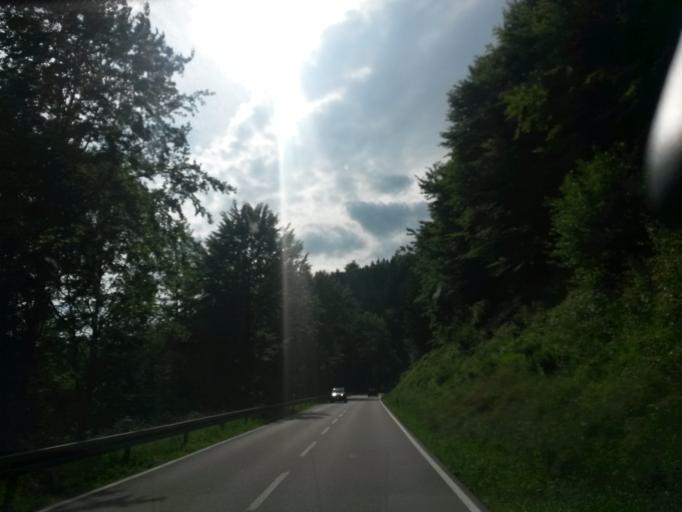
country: DE
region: Baden-Wuerttemberg
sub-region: Karlsruhe Region
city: Oberreichenbach
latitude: 48.7397
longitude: 8.6952
